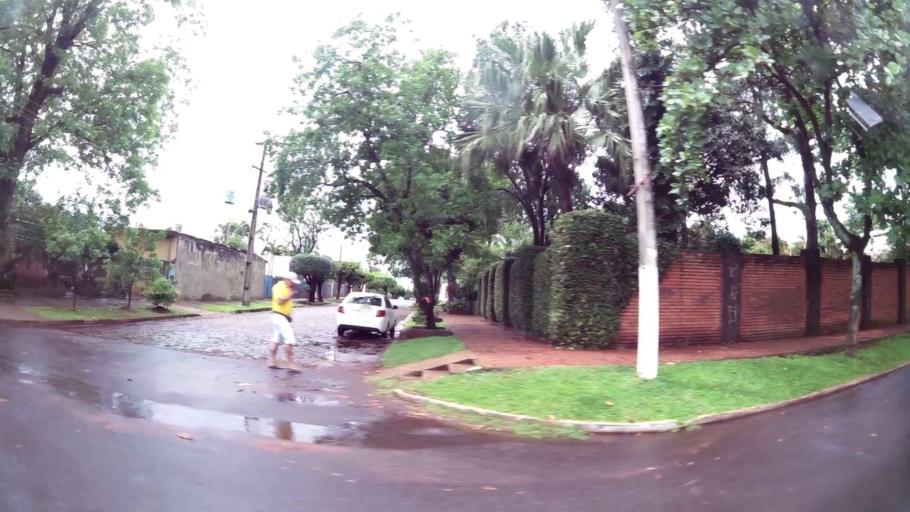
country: PY
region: Alto Parana
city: Ciudad del Este
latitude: -25.5026
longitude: -54.6583
